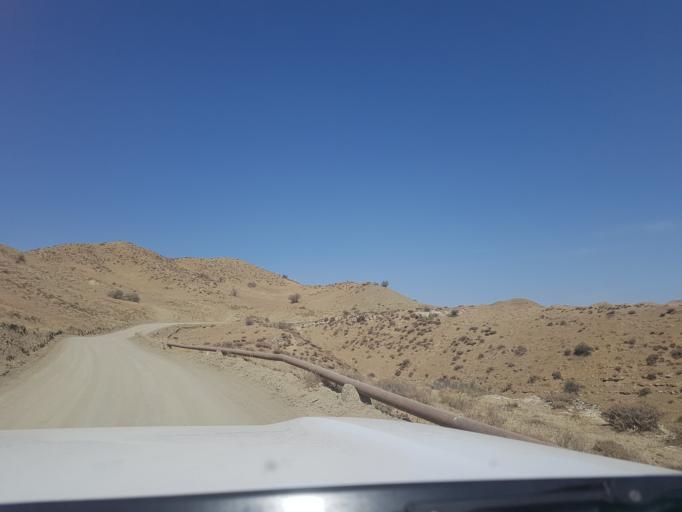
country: TM
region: Ahal
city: Baharly
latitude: 38.2415
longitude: 56.8902
